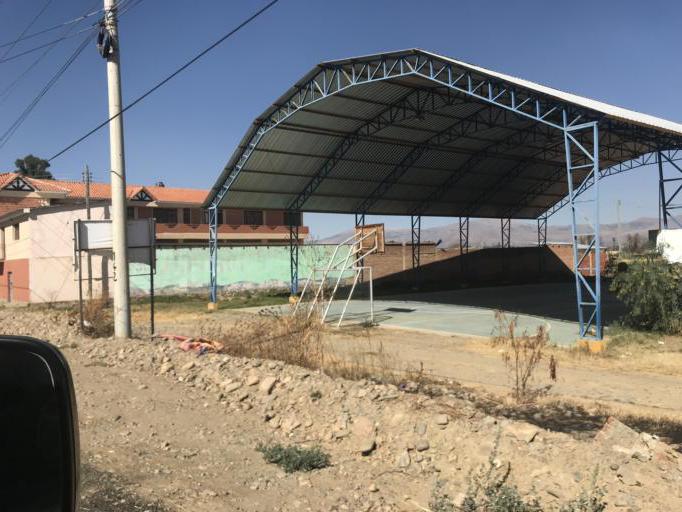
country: BO
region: Cochabamba
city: Punata
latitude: -17.5597
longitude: -65.8704
